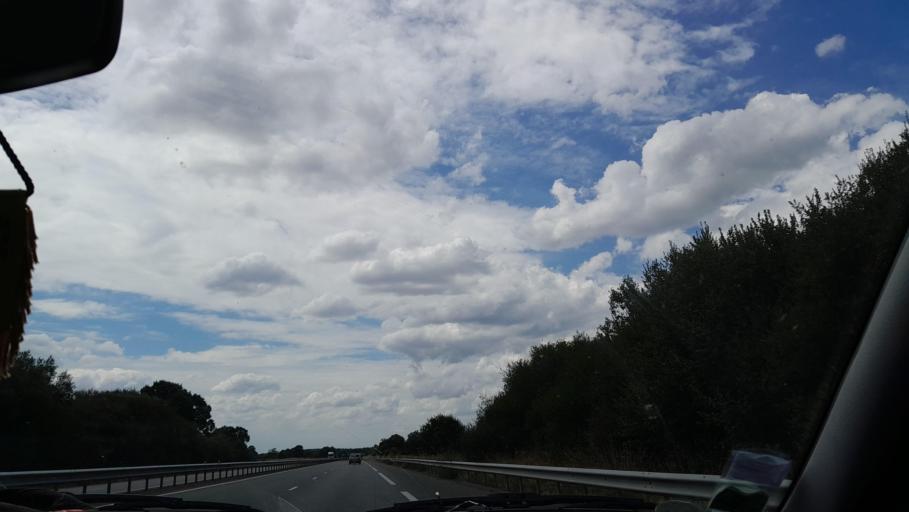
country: FR
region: Brittany
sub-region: Departement d'Ille-et-Vilaine
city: Romagne
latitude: 48.3549
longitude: -1.2577
